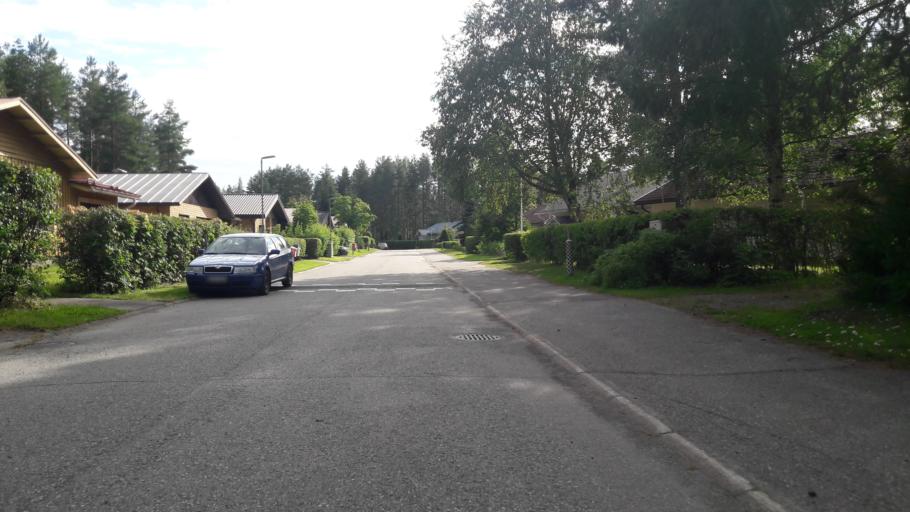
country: FI
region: North Karelia
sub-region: Joensuu
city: Joensuu
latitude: 62.6211
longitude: 29.7350
